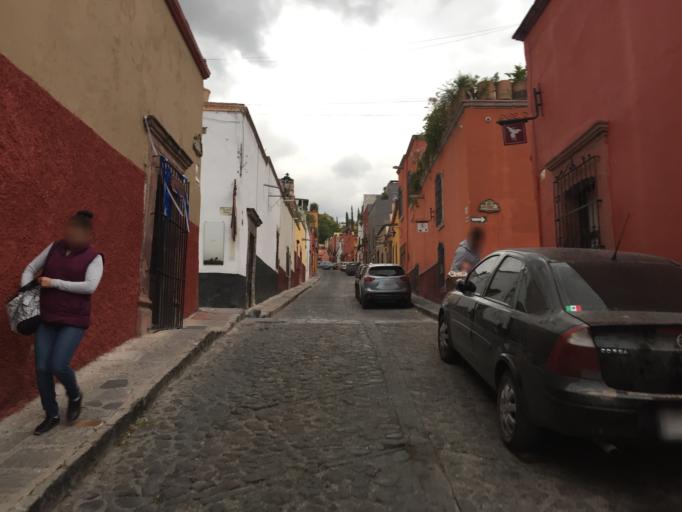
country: MX
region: Guanajuato
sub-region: San Miguel de Allende
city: San Miguel de Allende
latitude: 20.9113
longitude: -100.7437
